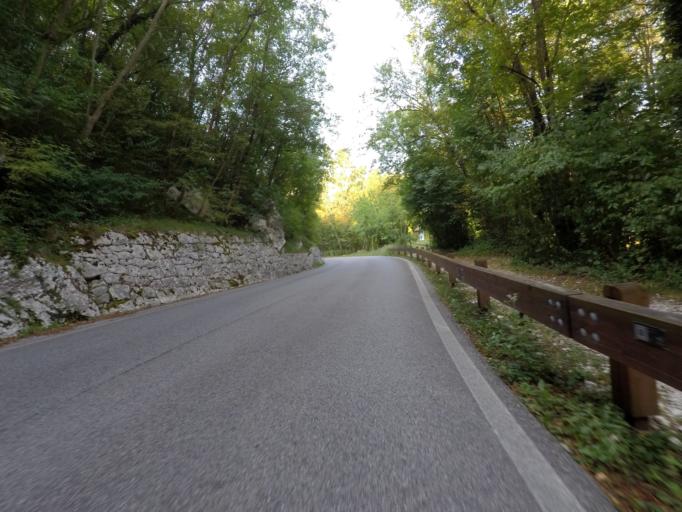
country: IT
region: Friuli Venezia Giulia
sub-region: Provincia di Udine
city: Forgaria nel Friuli
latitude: 46.2283
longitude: 13.0247
